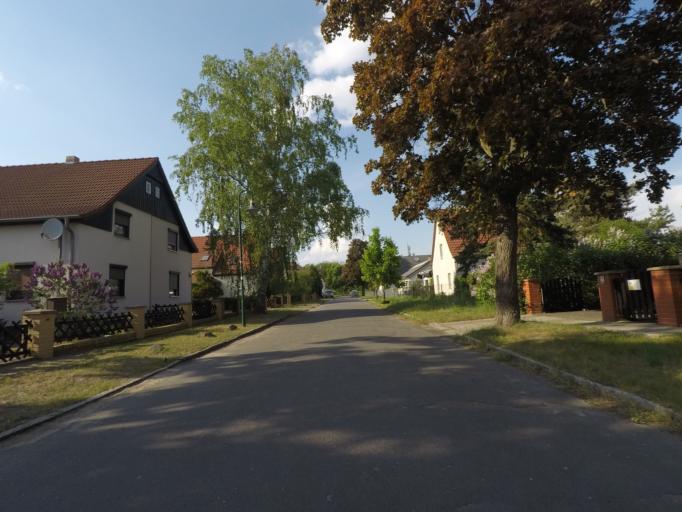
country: DE
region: Brandenburg
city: Melchow
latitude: 52.8380
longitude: 13.7231
